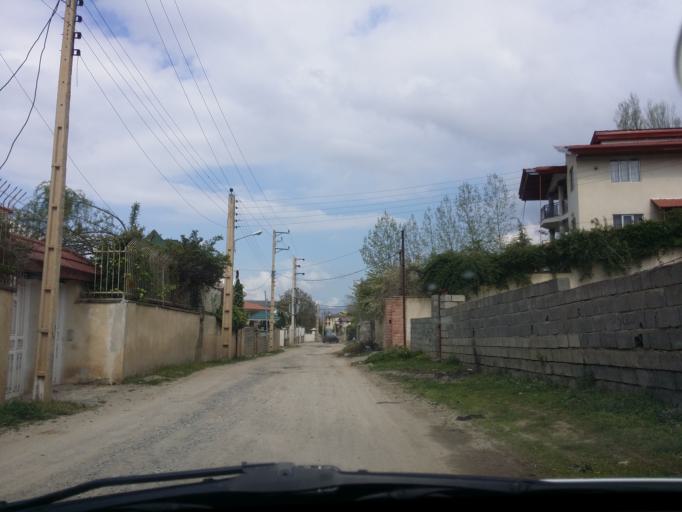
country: IR
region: Mazandaran
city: `Abbasabad
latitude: 36.4860
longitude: 51.1405
